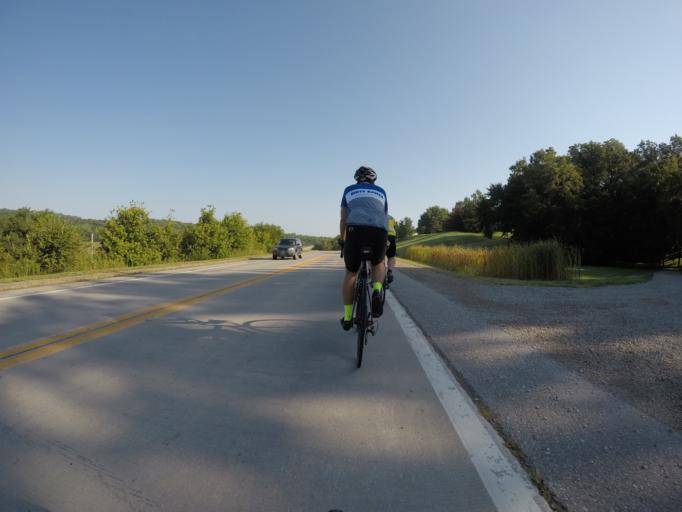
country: US
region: Missouri
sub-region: Platte County
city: Weston
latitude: 39.3775
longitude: -94.8640
